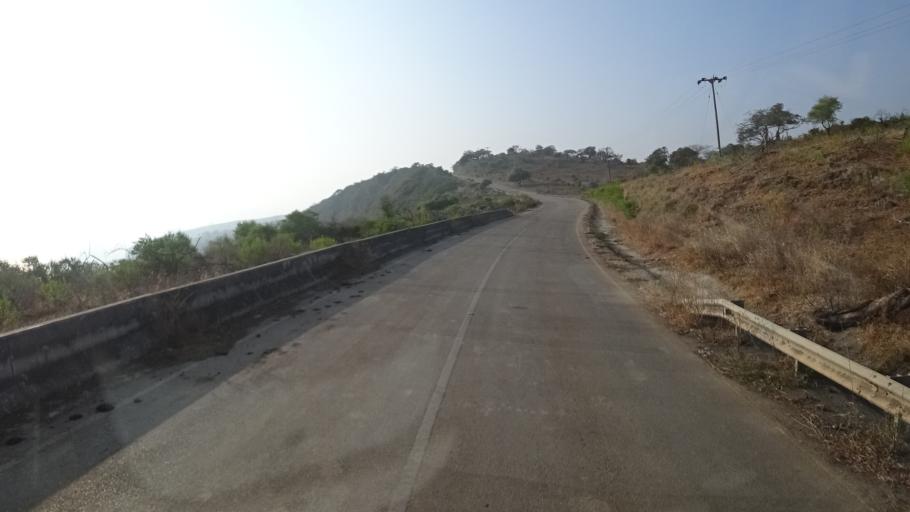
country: YE
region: Al Mahrah
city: Hawf
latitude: 16.7413
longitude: 53.3655
